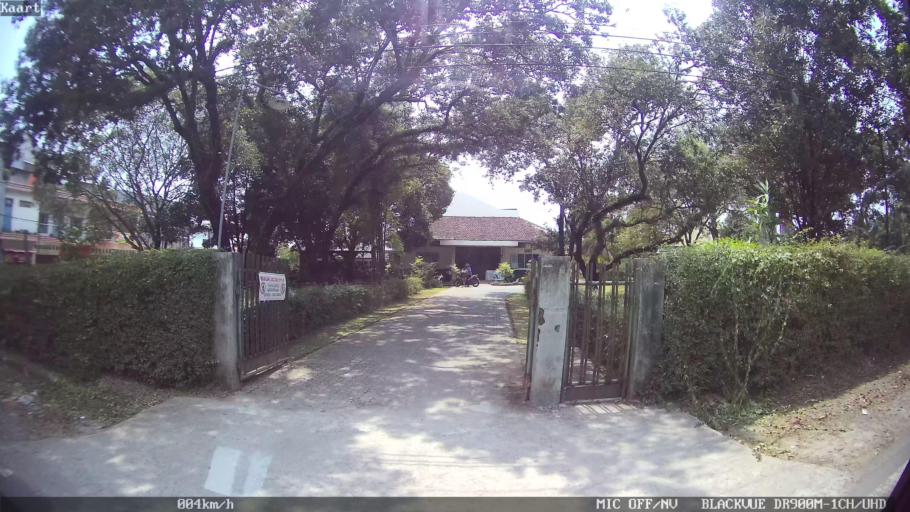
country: ID
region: Lampung
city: Pringsewu
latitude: -5.3579
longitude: 104.9771
